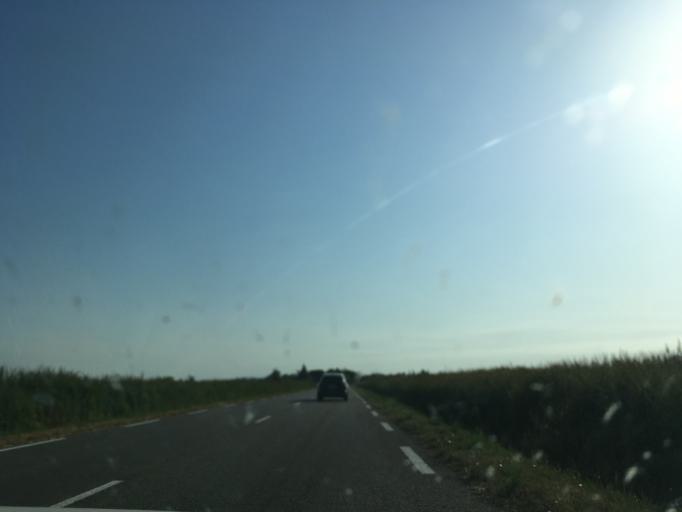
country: FR
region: Languedoc-Roussillon
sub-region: Departement du Gard
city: Fourques
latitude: 43.6415
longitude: 4.5631
